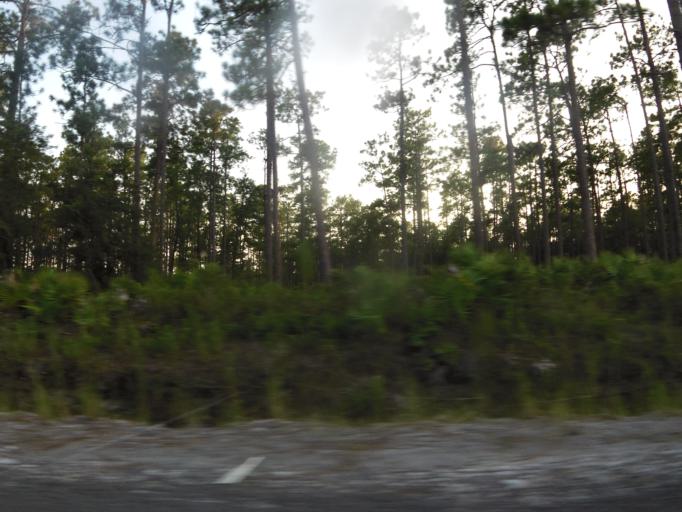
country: US
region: Florida
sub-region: Baker County
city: Macclenny
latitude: 30.3894
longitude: -82.0836
